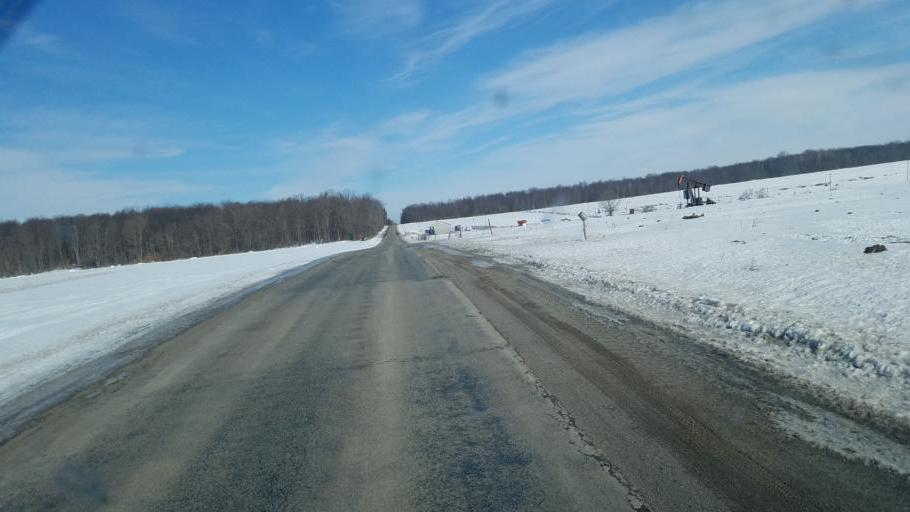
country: US
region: New York
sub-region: Allegany County
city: Andover
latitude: 42.0642
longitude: -77.7720
